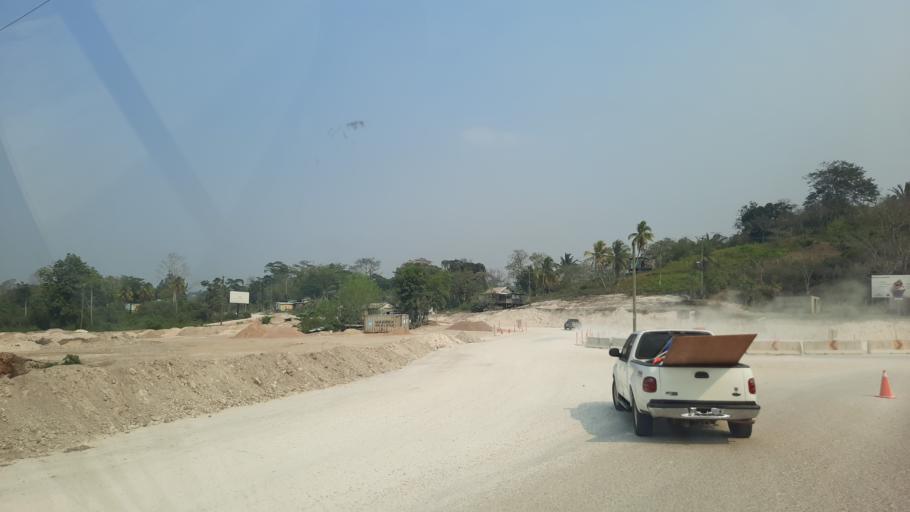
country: BZ
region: Cayo
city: Valley of Peace
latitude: 17.2259
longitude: -88.9225
